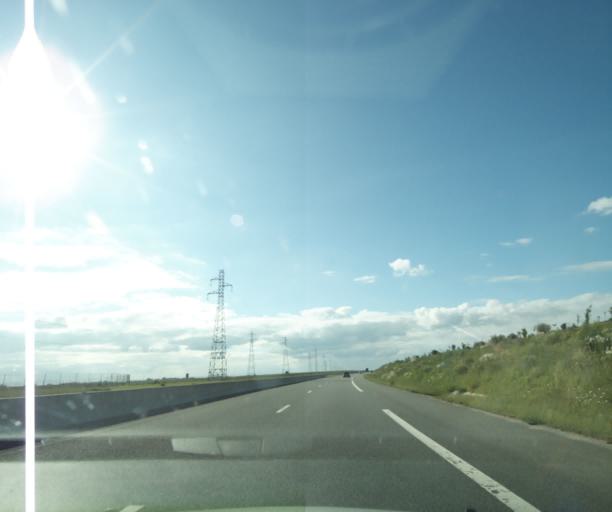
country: FR
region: Centre
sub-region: Departement d'Eure-et-Loir
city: Voves
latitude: 48.3294
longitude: 1.6495
